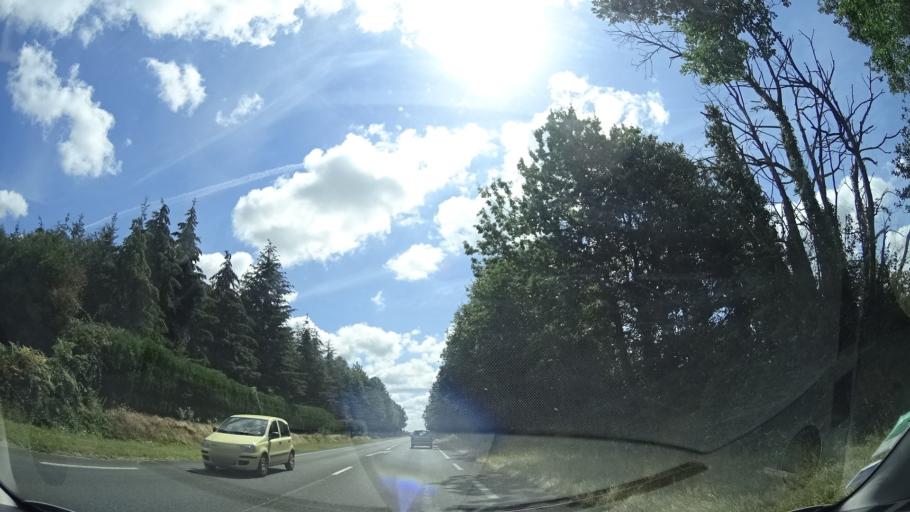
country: FR
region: Pays de la Loire
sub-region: Departement de la Sarthe
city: La Fleche
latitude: 47.7356
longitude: -0.1254
